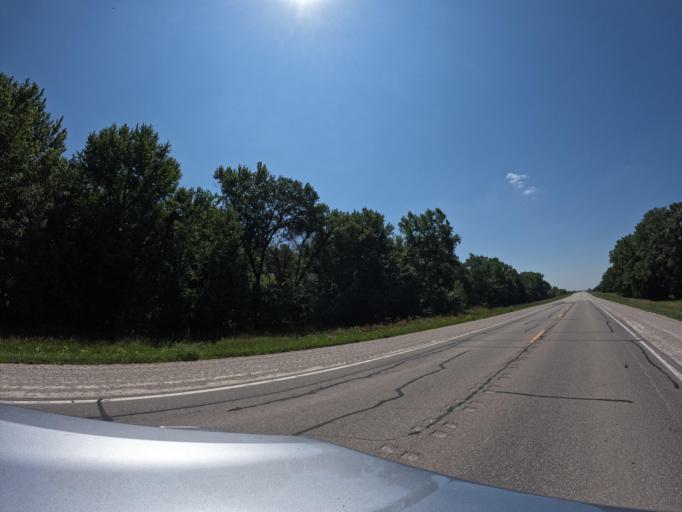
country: US
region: Iowa
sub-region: Keokuk County
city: Sigourney
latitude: 41.3051
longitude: -92.2048
